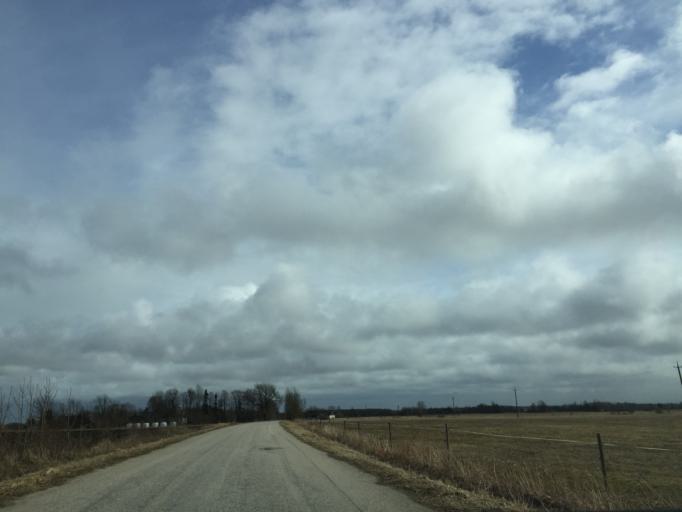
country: EE
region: Laeaene
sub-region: Lihula vald
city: Lihula
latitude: 58.7355
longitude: 23.8412
